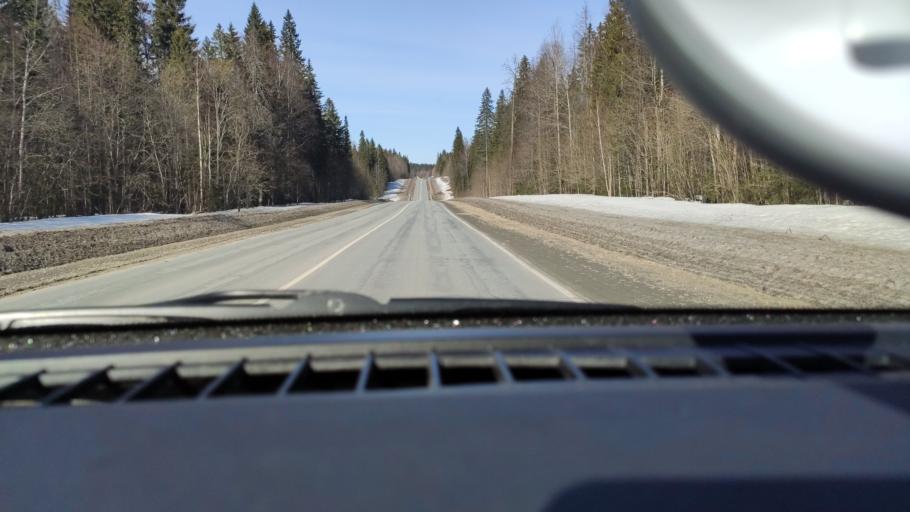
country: RU
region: Perm
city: Perm
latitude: 58.1890
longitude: 56.2169
